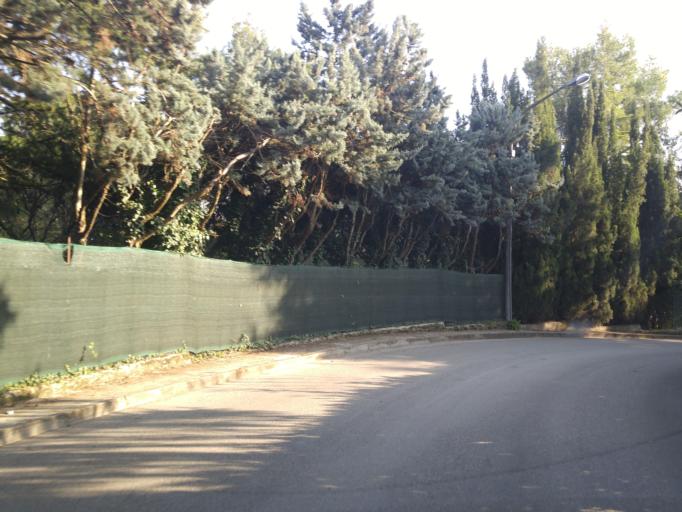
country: IT
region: The Marches
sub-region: Provincia di Pesaro e Urbino
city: Calcinelli
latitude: 43.7531
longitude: 12.9169
